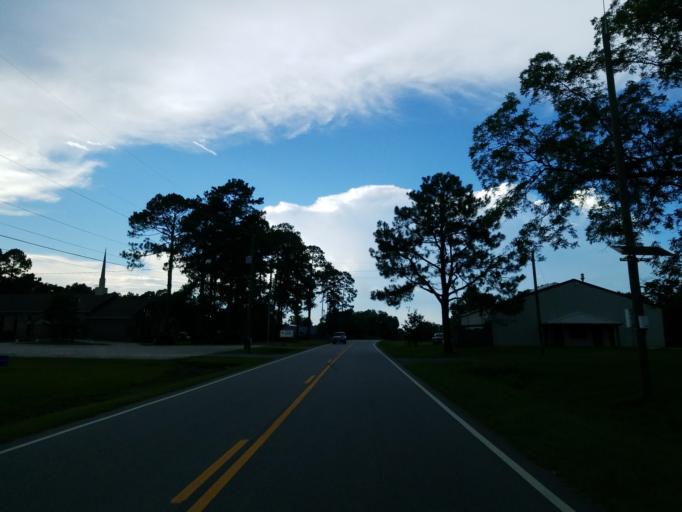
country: US
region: Georgia
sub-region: Tift County
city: Unionville
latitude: 31.3552
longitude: -83.4855
